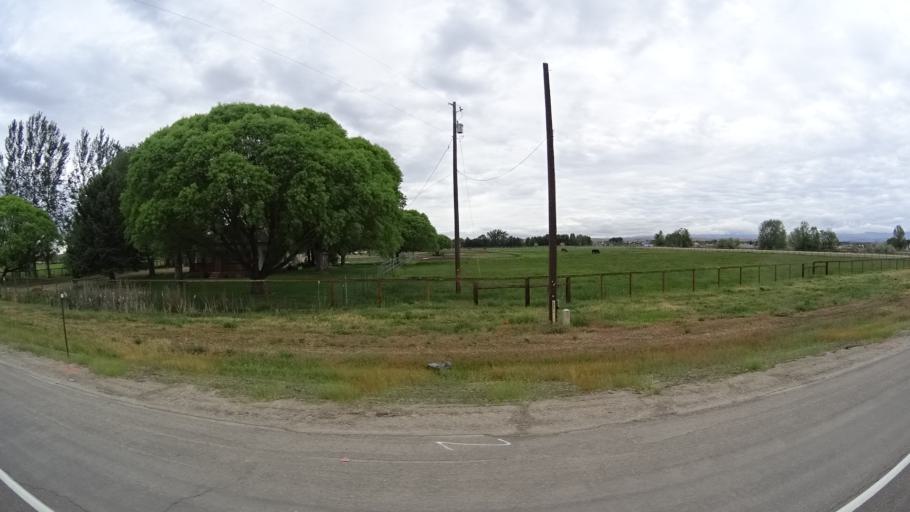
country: US
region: Idaho
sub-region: Ada County
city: Star
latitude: 43.6918
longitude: -116.4551
